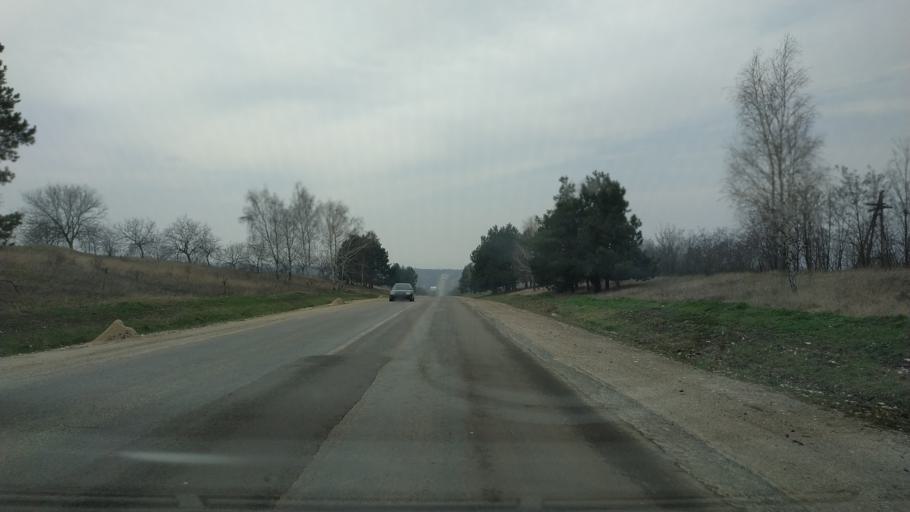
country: MD
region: Cahul
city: Cahul
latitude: 45.9315
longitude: 28.2736
